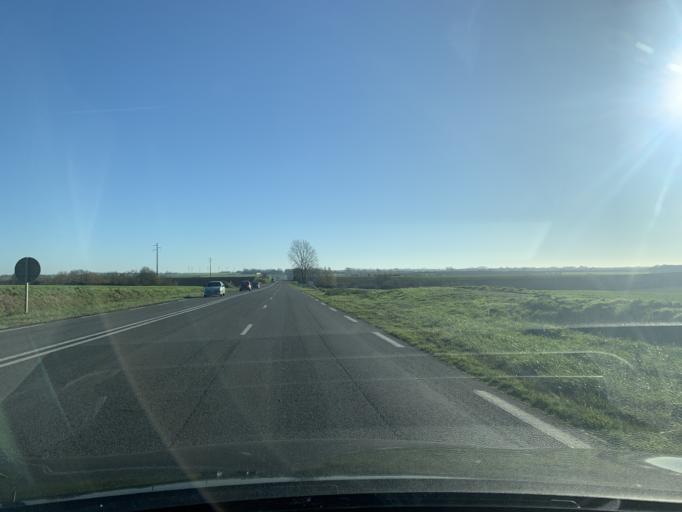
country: FR
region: Nord-Pas-de-Calais
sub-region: Departement du Nord
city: Escaudoeuvres
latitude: 50.1617
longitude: 3.2915
